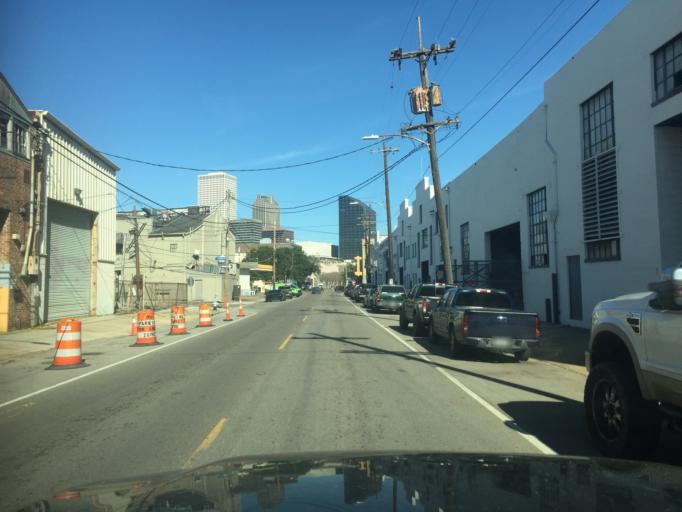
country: US
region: Louisiana
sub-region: Orleans Parish
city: New Orleans
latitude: 29.9409
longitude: -90.0672
